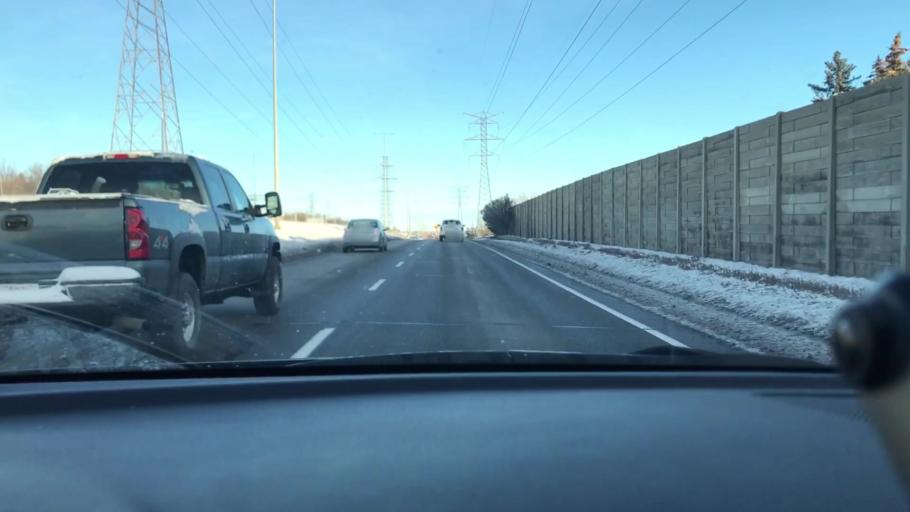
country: CA
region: Alberta
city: Calgary
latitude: 51.0470
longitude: -114.1642
